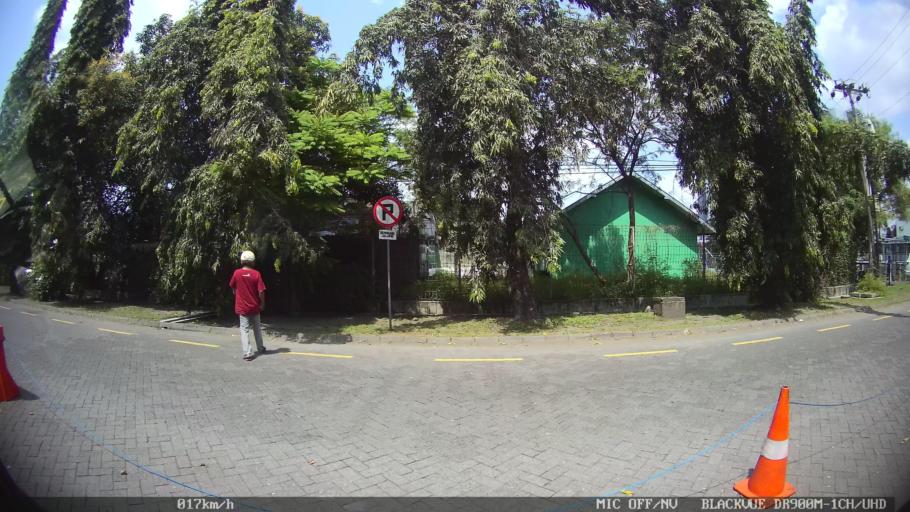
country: ID
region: Daerah Istimewa Yogyakarta
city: Yogyakarta
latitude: -7.7707
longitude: 110.3725
